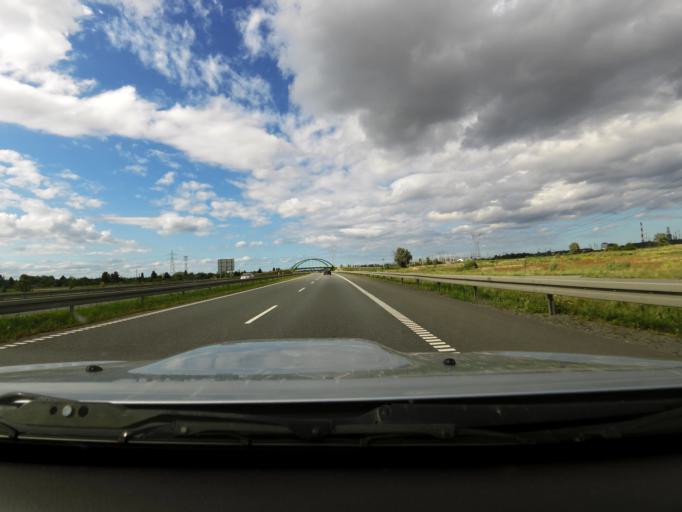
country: PL
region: Pomeranian Voivodeship
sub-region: Gdansk
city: Gdansk
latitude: 54.3276
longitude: 18.7052
